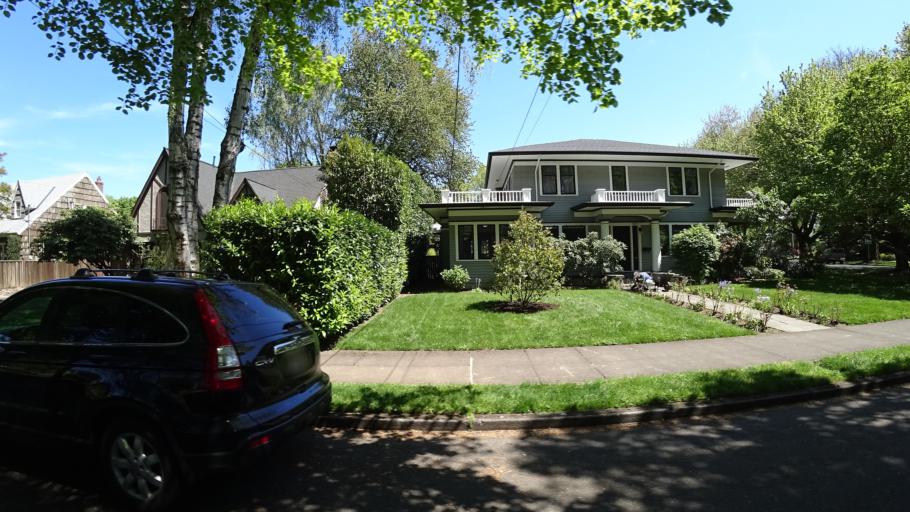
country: US
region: Oregon
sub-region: Clackamas County
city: Milwaukie
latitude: 45.4663
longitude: -122.6293
